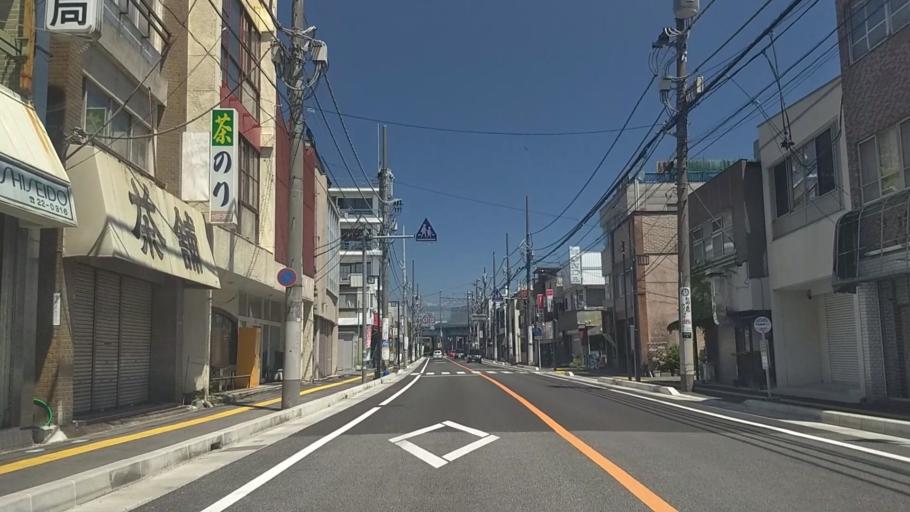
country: JP
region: Yamanashi
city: Nirasaki
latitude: 35.7092
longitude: 138.4502
